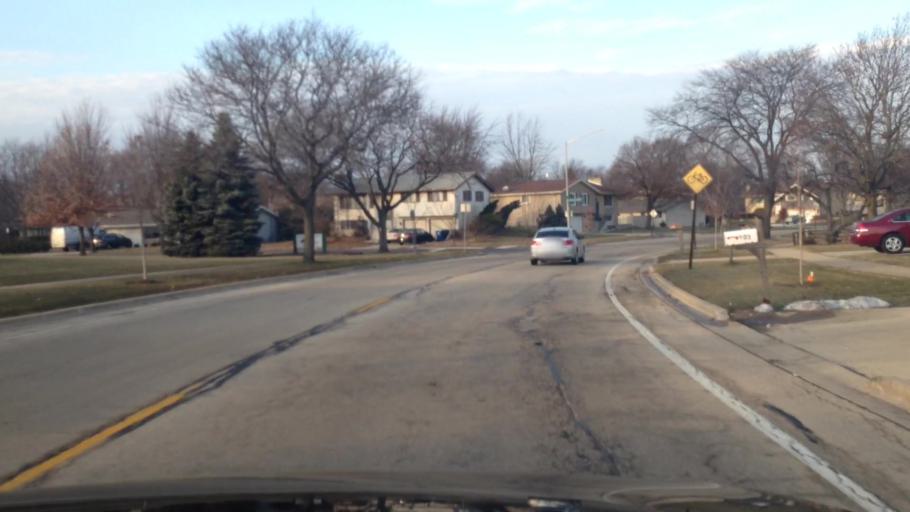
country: US
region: Illinois
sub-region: Cook County
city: Schaumburg
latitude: 42.0092
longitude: -88.1023
